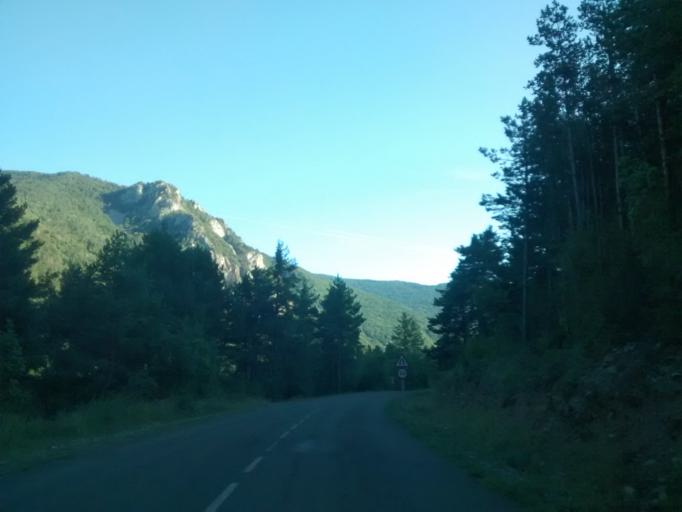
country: ES
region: Aragon
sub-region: Provincia de Huesca
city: Anso
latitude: 42.7930
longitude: -0.7359
